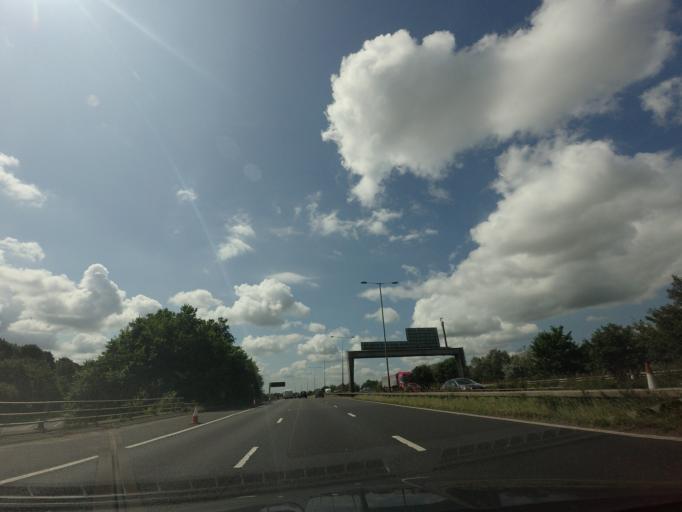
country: GB
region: England
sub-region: Lancashire
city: Clayton-le-Woods
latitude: 53.7116
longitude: -2.6700
